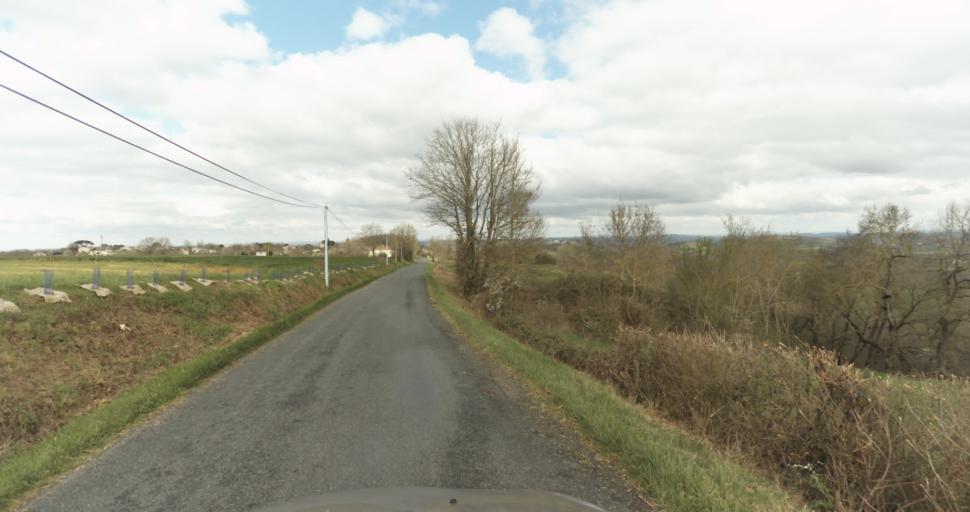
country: FR
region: Midi-Pyrenees
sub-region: Departement du Tarn
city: Frejairolles
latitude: 43.8678
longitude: 2.2028
